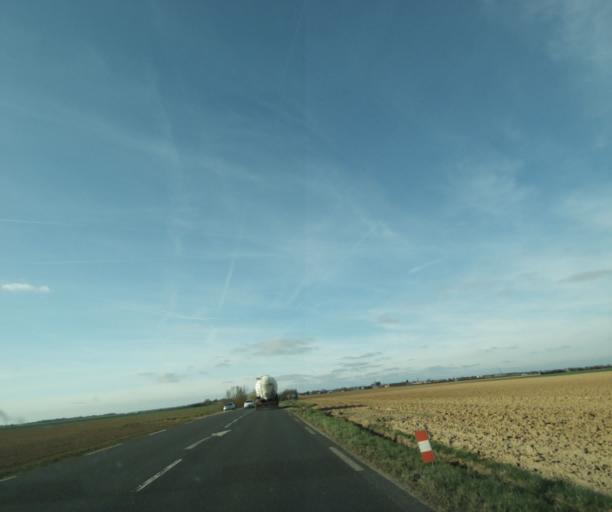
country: FR
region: Ile-de-France
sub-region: Departement des Yvelines
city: Ablis
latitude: 48.5020
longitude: 1.8388
